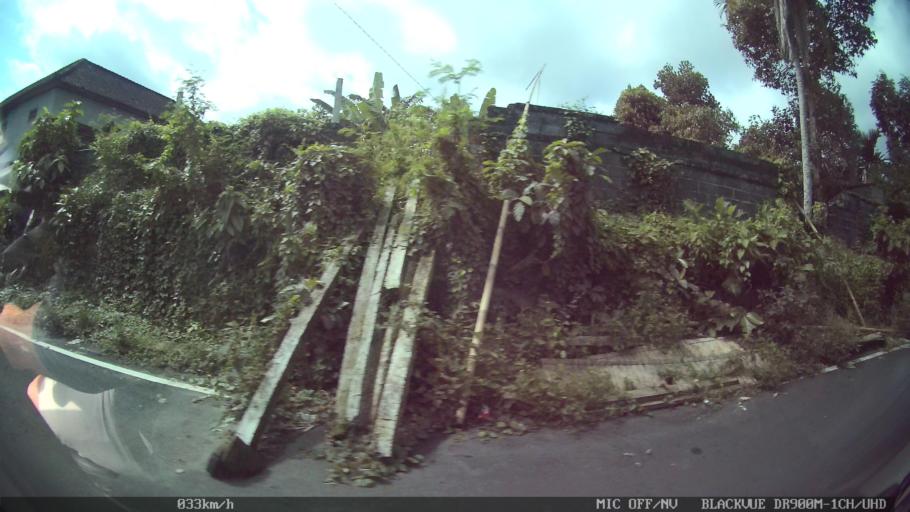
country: ID
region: Bali
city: Banjar Pesalakan
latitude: -8.5212
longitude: 115.3104
